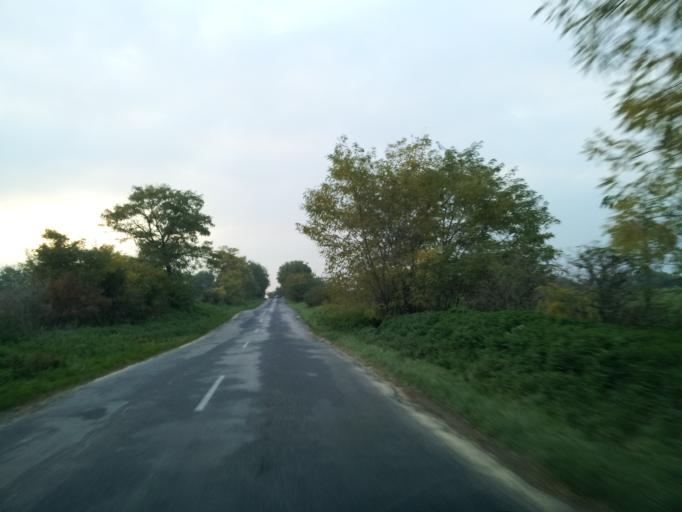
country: HU
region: Gyor-Moson-Sopron
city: Bakonyszentlaszlo
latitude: 47.4697
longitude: 17.8674
